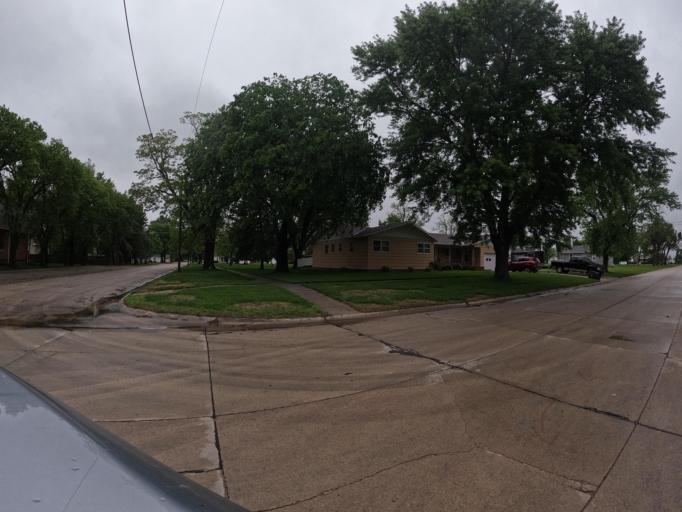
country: US
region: Nebraska
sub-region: Clay County
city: Harvard
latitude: 40.6227
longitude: -98.0944
